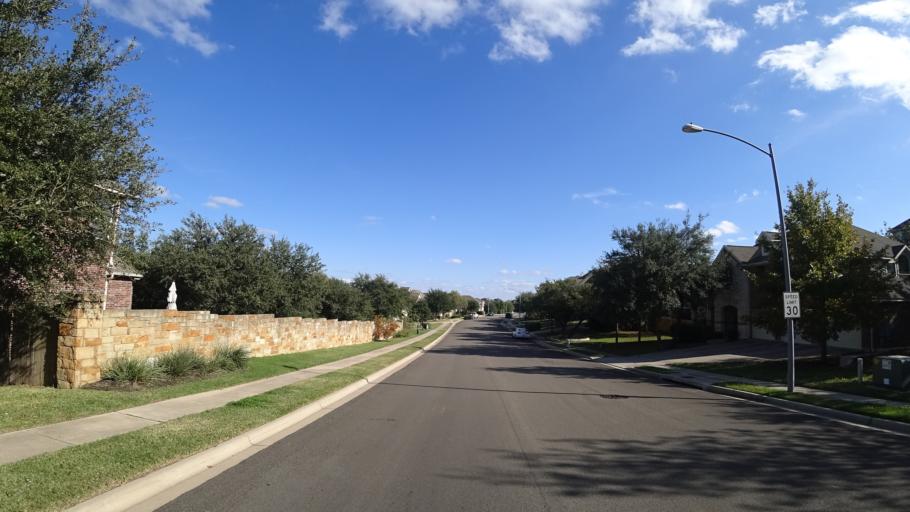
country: US
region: Texas
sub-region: Travis County
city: Barton Creek
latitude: 30.2482
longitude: -97.8747
